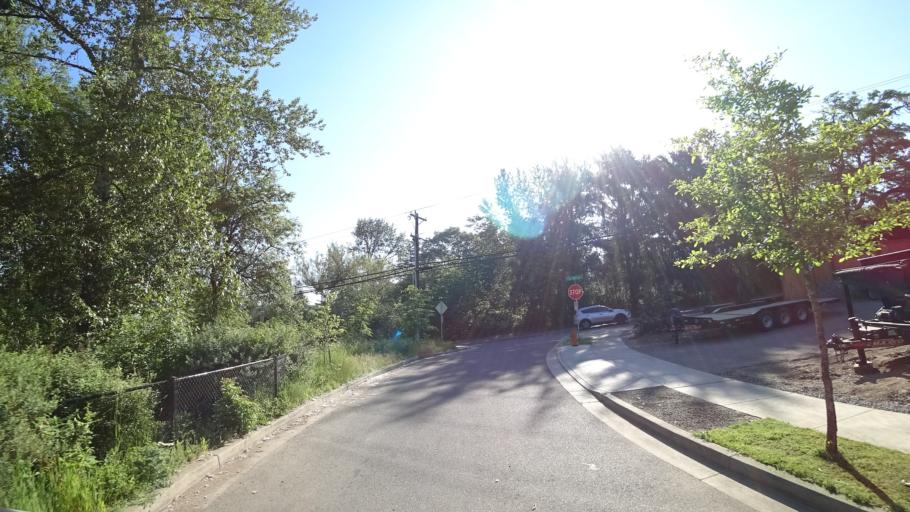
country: US
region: Oregon
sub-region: Multnomah County
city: Lents
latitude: 45.4732
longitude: -122.5484
